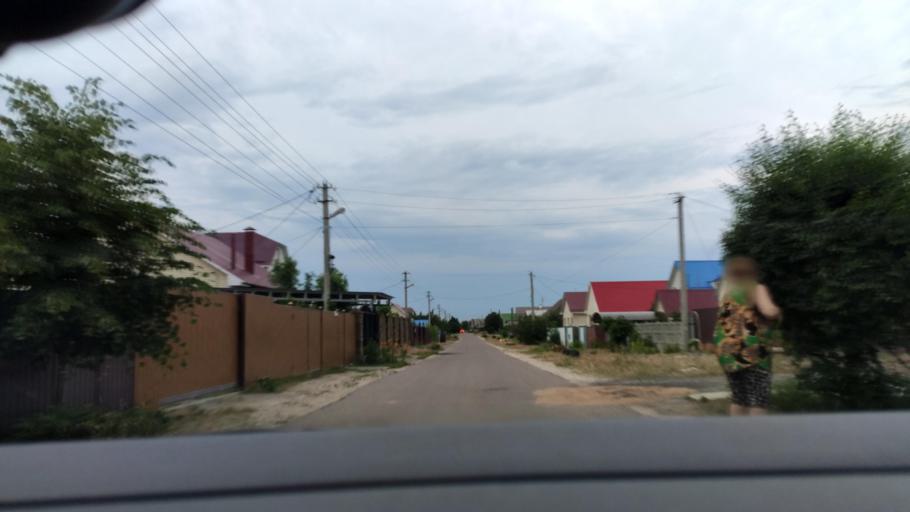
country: RU
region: Voronezj
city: Maslovka
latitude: 51.5694
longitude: 39.2503
